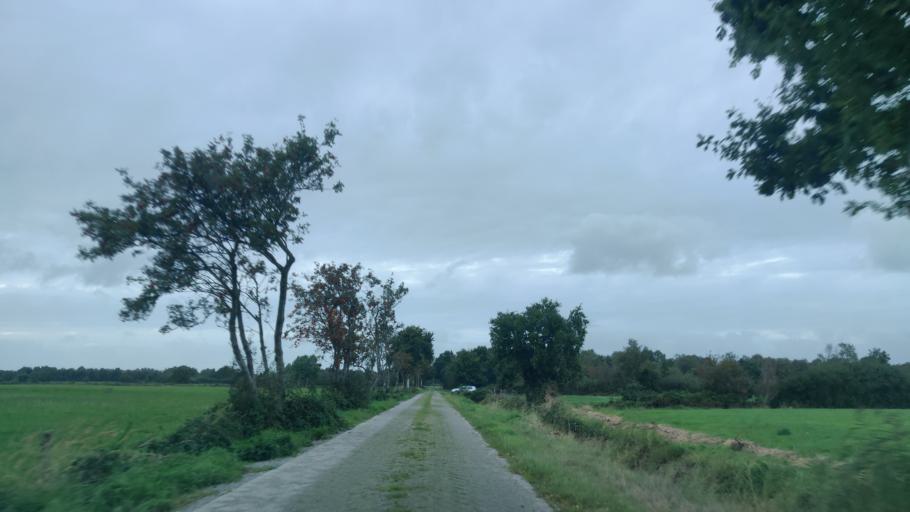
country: DE
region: Lower Saxony
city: Aurich
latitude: 53.5290
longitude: 7.4731
